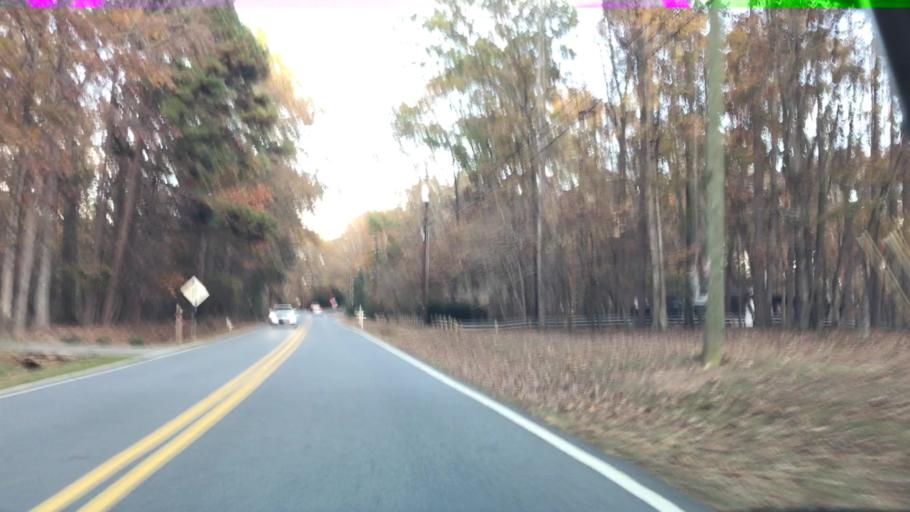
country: US
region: Georgia
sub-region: Gwinnett County
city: Suwanee
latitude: 34.0713
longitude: -84.0873
